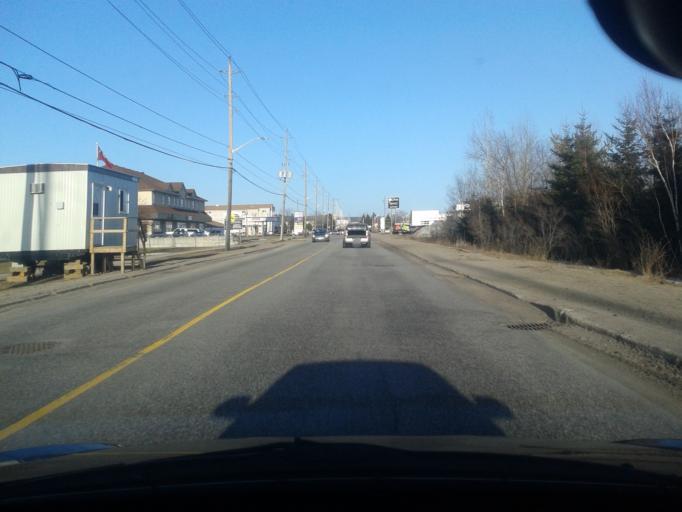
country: CA
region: Ontario
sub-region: Nipissing District
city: North Bay
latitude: 46.3325
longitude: -79.4833
